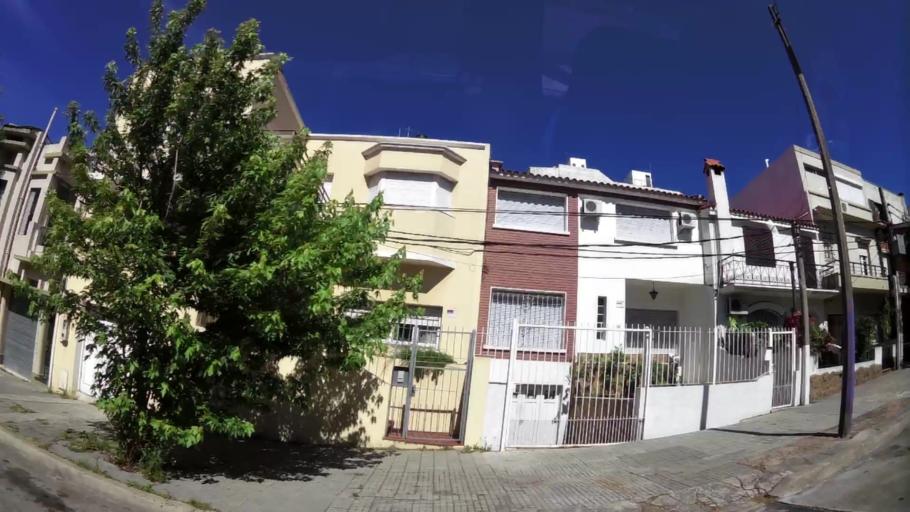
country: UY
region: Montevideo
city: Montevideo
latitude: -34.9163
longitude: -56.1639
